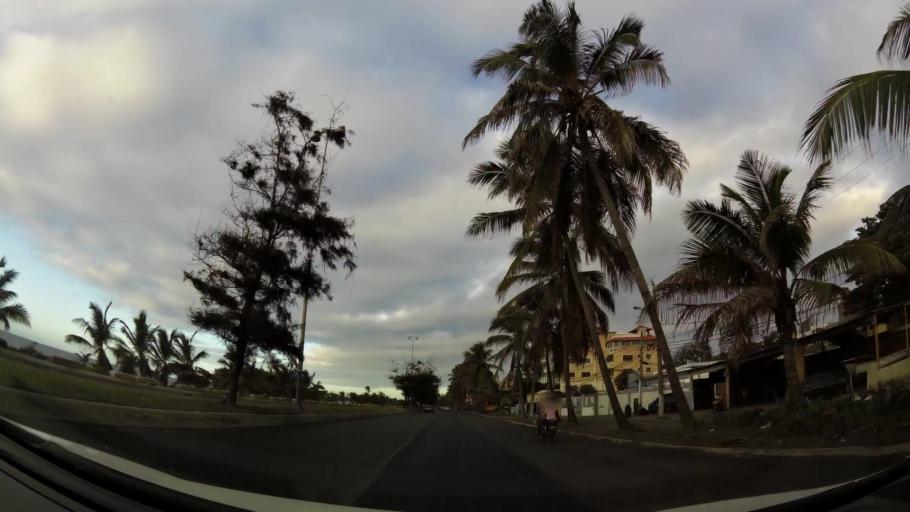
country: DO
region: Nacional
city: Bella Vista
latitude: 18.4312
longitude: -69.9588
